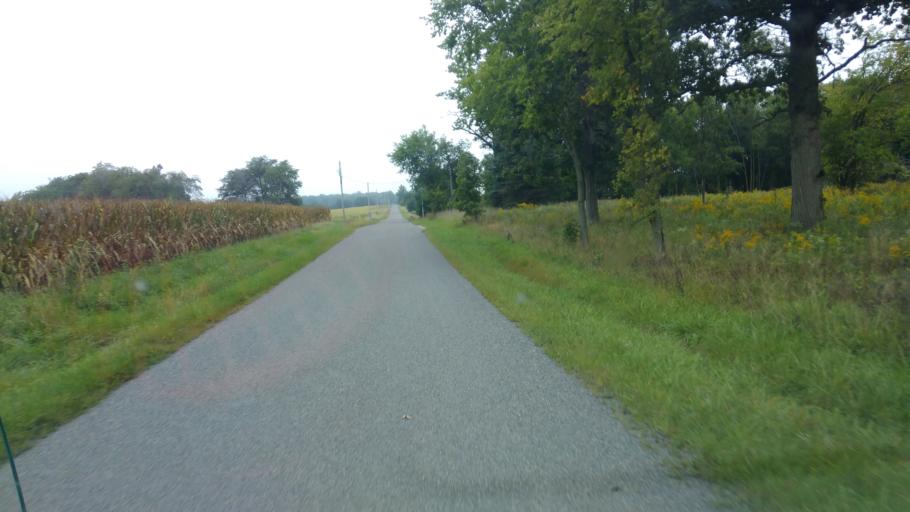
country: US
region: Ohio
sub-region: Logan County
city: Northwood
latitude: 40.4546
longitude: -83.5667
